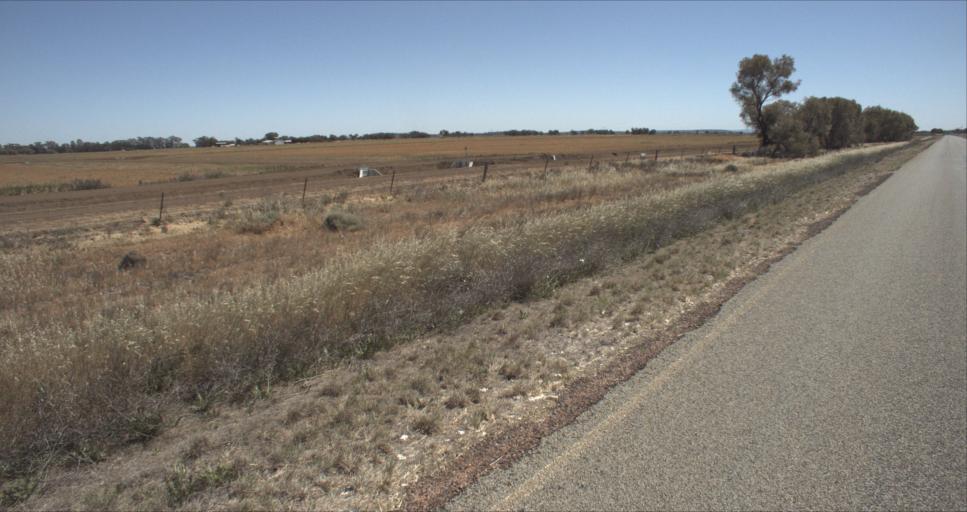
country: AU
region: New South Wales
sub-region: Leeton
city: Leeton
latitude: -34.4618
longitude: 146.2940
